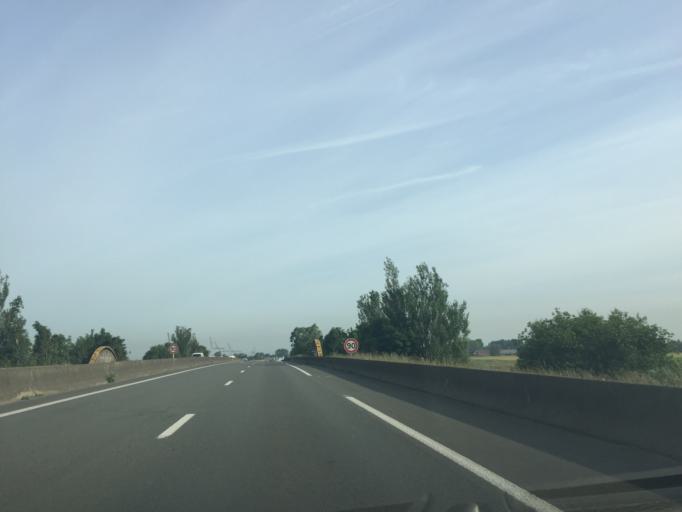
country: FR
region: Nord-Pas-de-Calais
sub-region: Departement du Nord
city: Loon-Plage
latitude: 50.9866
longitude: 2.2074
